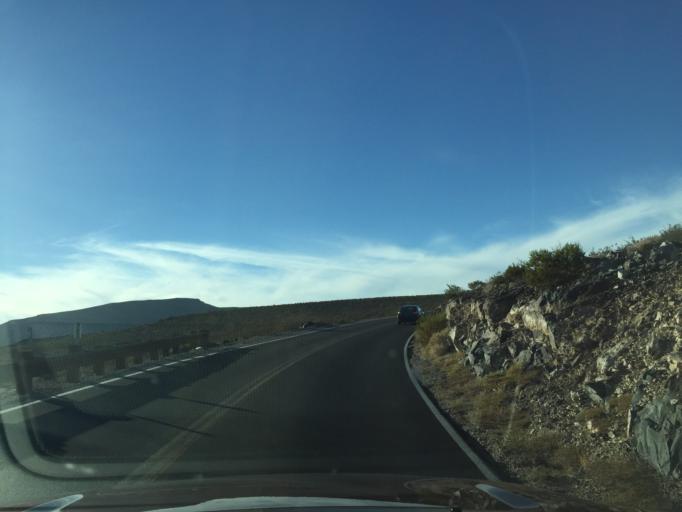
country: US
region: California
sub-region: Inyo County
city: Lone Pine
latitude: 36.3490
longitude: -117.5490
